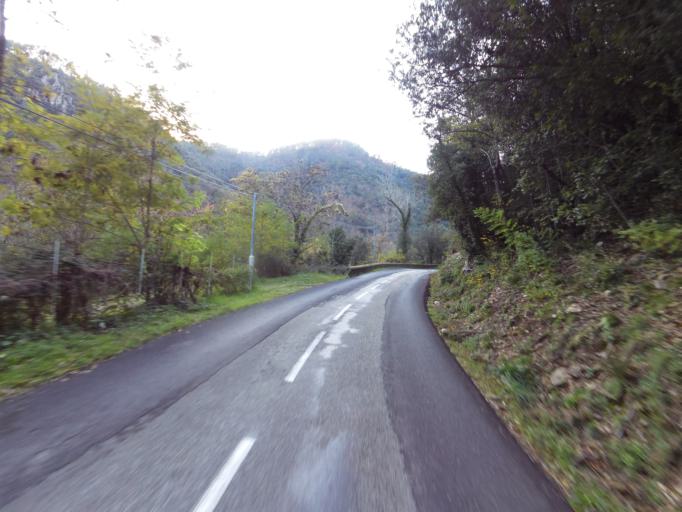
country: FR
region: Rhone-Alpes
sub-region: Departement de l'Ardeche
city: Joyeuse
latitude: 44.5120
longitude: 4.2021
